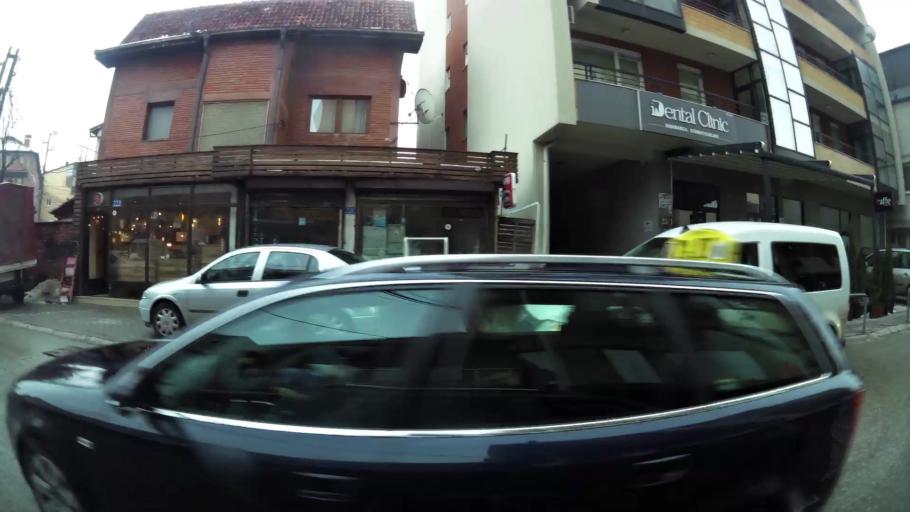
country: XK
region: Pristina
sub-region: Komuna e Prishtines
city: Pristina
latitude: 42.6680
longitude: 21.1622
